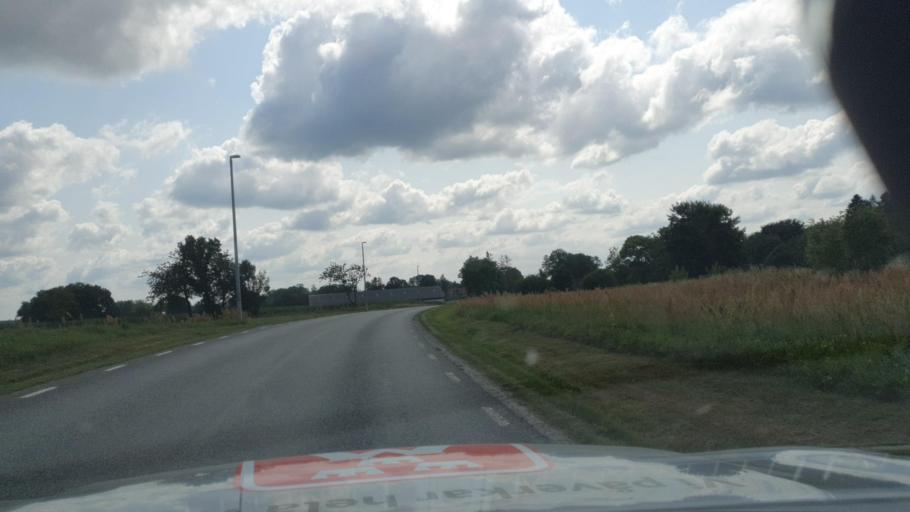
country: SE
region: Skane
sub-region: Hassleholms Kommun
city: Vinslov
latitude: 56.0594
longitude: 13.8358
